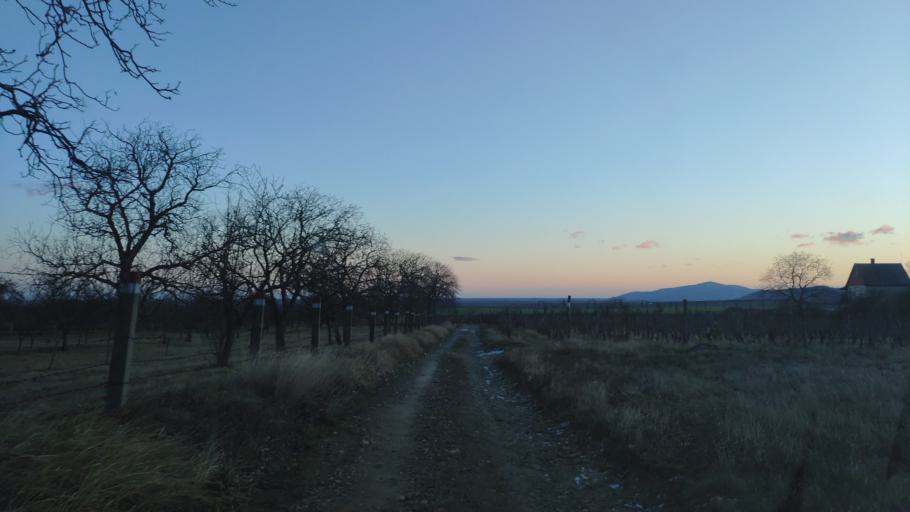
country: HU
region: Borsod-Abauj-Zemplen
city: Olaszliszka
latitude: 48.2713
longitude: 21.3985
